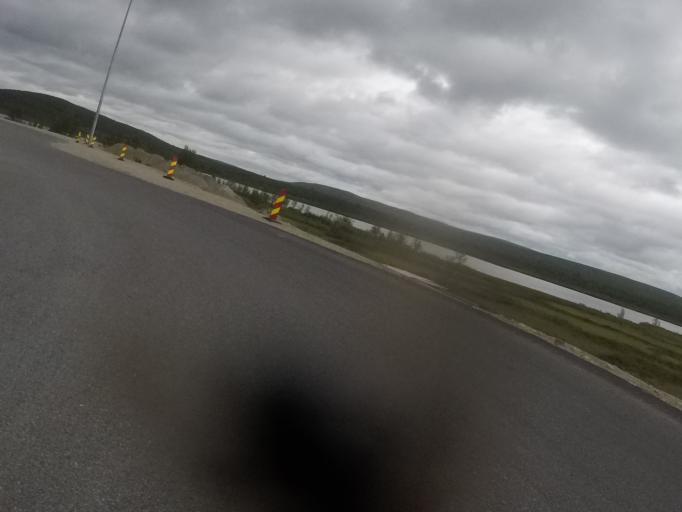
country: FI
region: Lapland
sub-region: Tunturi-Lappi
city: Enontekioe
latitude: 68.6592
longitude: 23.3245
